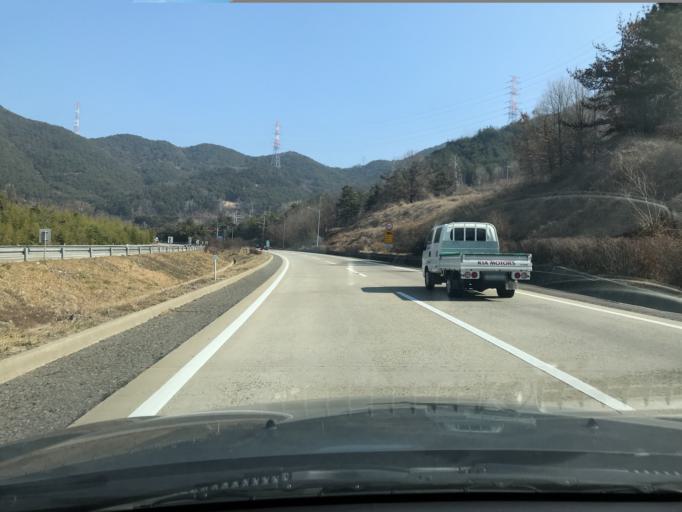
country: KR
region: Daegu
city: Hwawon
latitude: 35.7290
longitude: 128.4750
